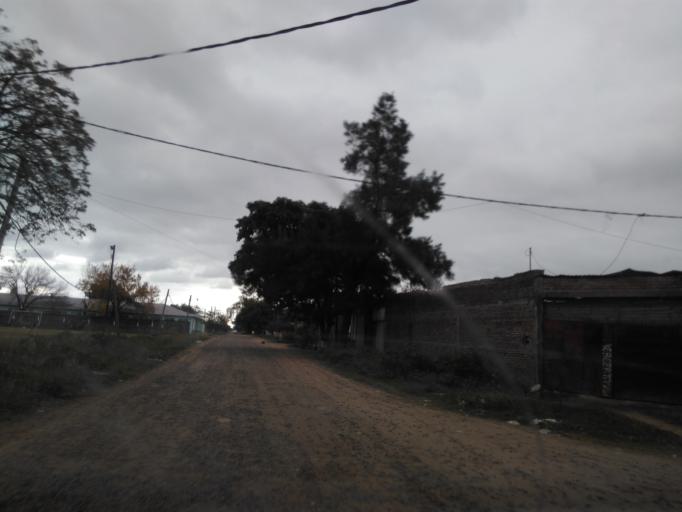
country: AR
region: Chaco
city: Fontana
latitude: -27.4548
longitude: -59.0351
